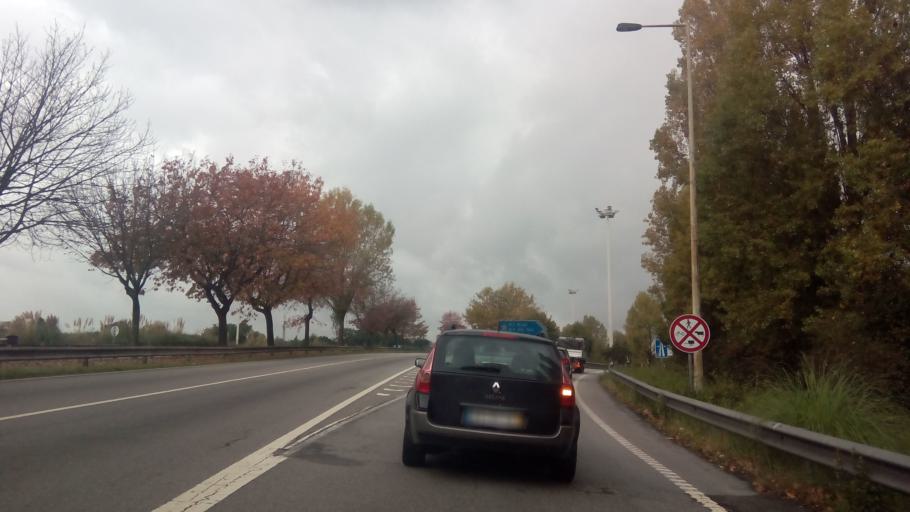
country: PT
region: Porto
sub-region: Maia
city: Pedroucos
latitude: 41.1802
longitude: -8.5912
